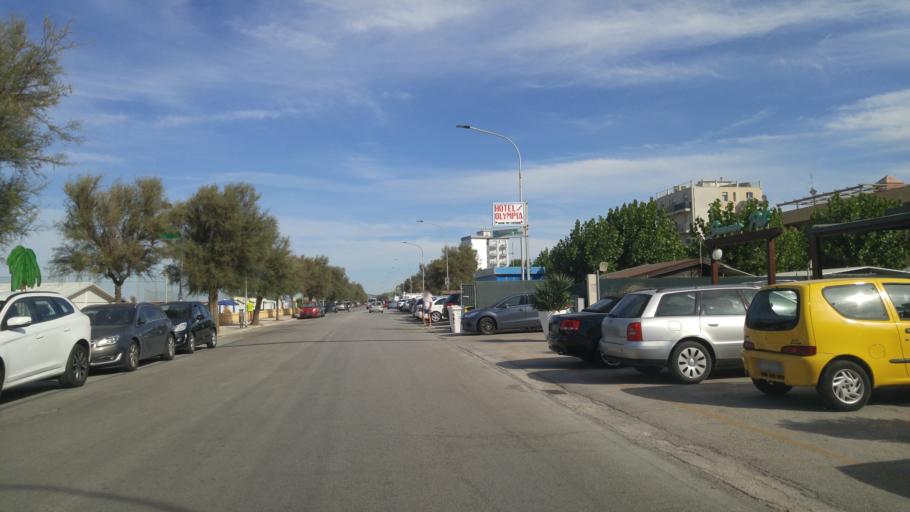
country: IT
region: The Marches
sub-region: Provincia di Ancona
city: Montignano-Marzocca
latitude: 43.6937
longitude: 13.2592
